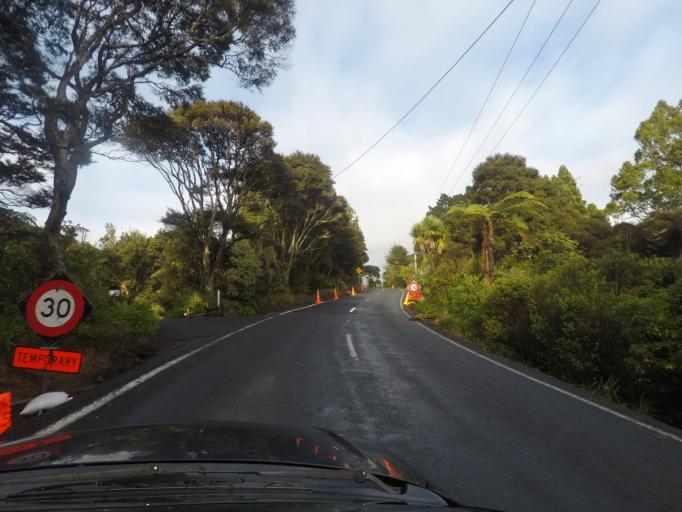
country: NZ
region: Auckland
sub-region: Auckland
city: Waitakere
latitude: -36.9164
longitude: 174.5976
